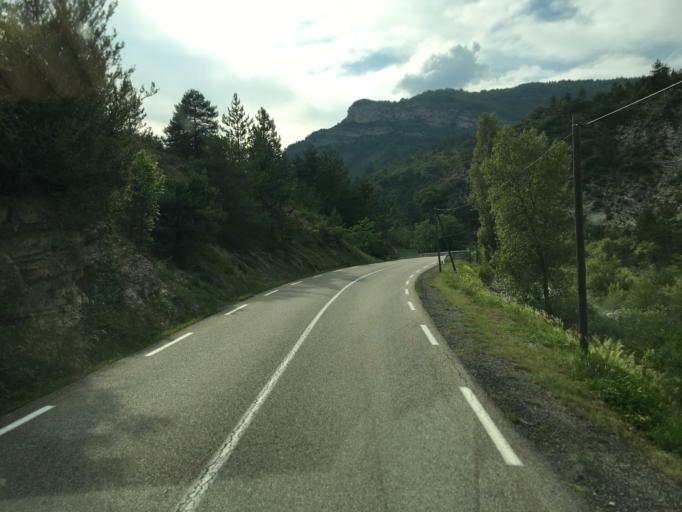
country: FR
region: Rhone-Alpes
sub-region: Departement de la Drome
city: Buis-les-Baronnies
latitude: 44.3892
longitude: 5.3862
